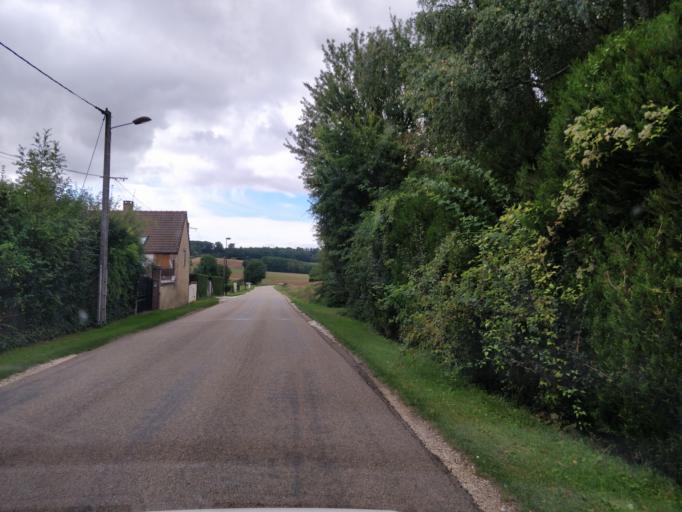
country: FR
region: Champagne-Ardenne
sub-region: Departement de l'Aube
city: Aix-en-Othe
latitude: 48.1608
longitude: 3.6343
